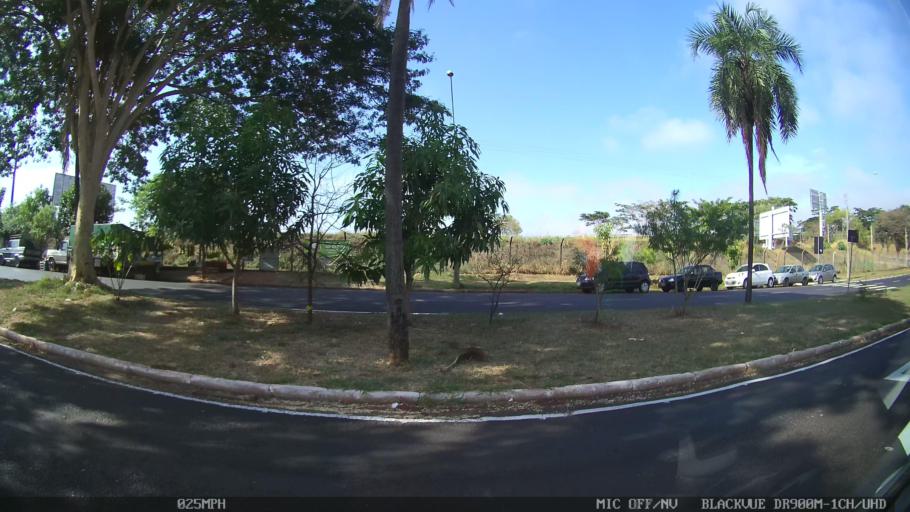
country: BR
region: Sao Paulo
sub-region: Sao Jose Do Rio Preto
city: Sao Jose do Rio Preto
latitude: -20.8221
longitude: -49.4174
